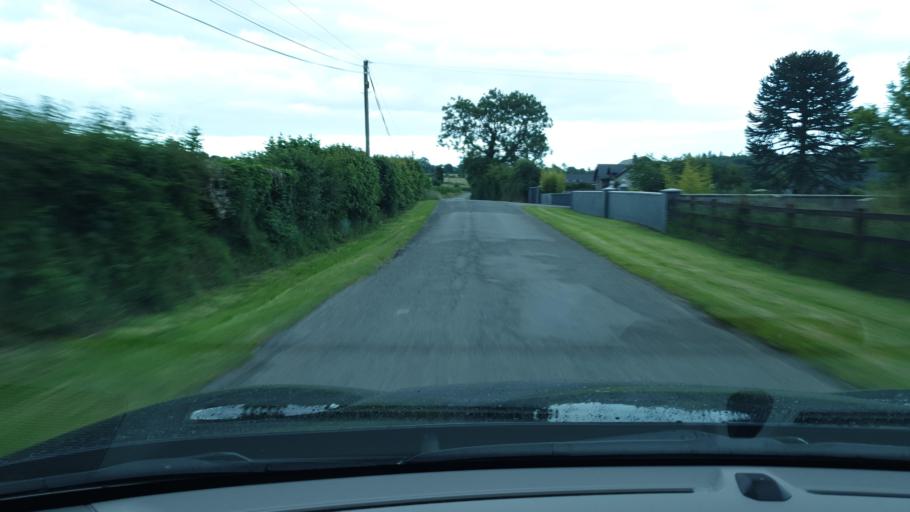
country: IE
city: Kentstown
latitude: 53.5992
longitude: -6.5907
